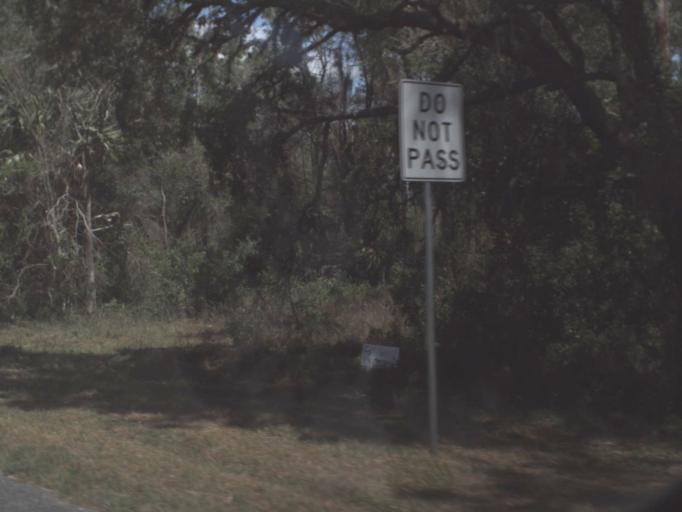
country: US
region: Florida
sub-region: Marion County
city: Silver Springs Shores
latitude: 29.2023
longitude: -81.9356
